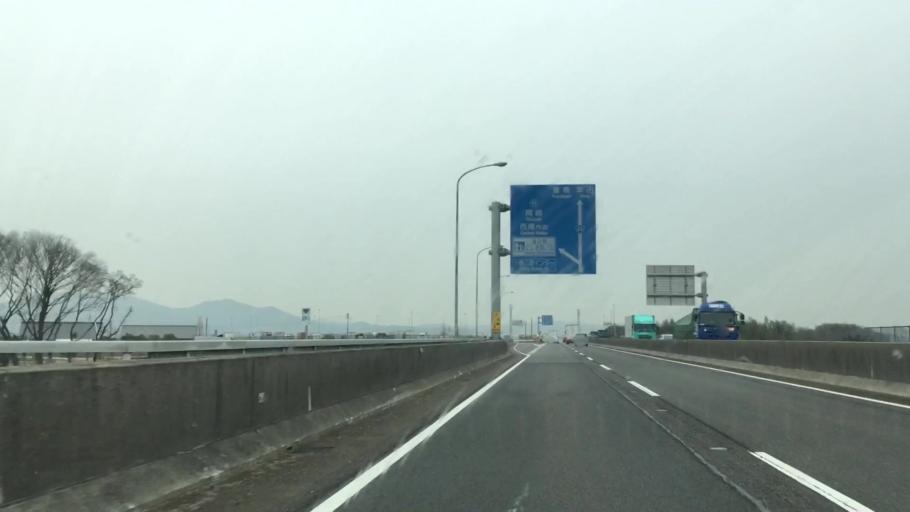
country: JP
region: Aichi
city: Nishio
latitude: 34.8787
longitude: 137.0805
